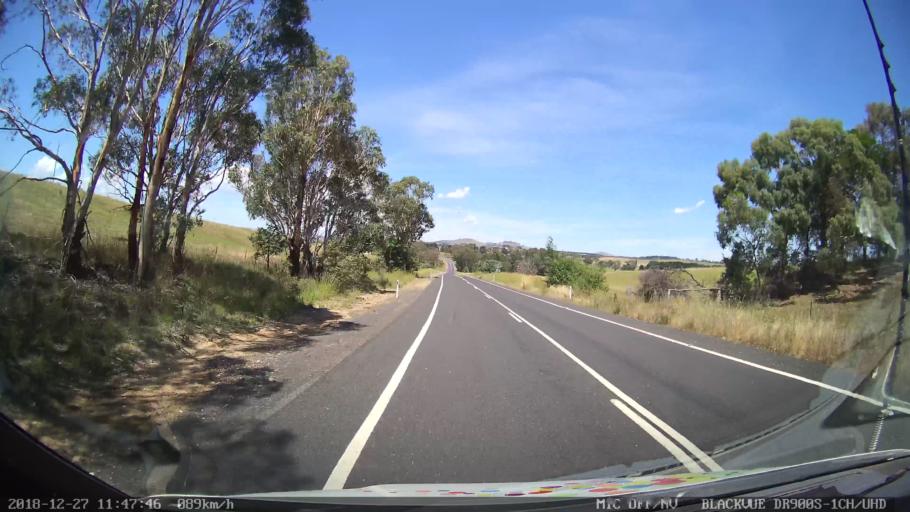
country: AU
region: New South Wales
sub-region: Bathurst Regional
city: Perthville
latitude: -33.5987
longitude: 149.4411
